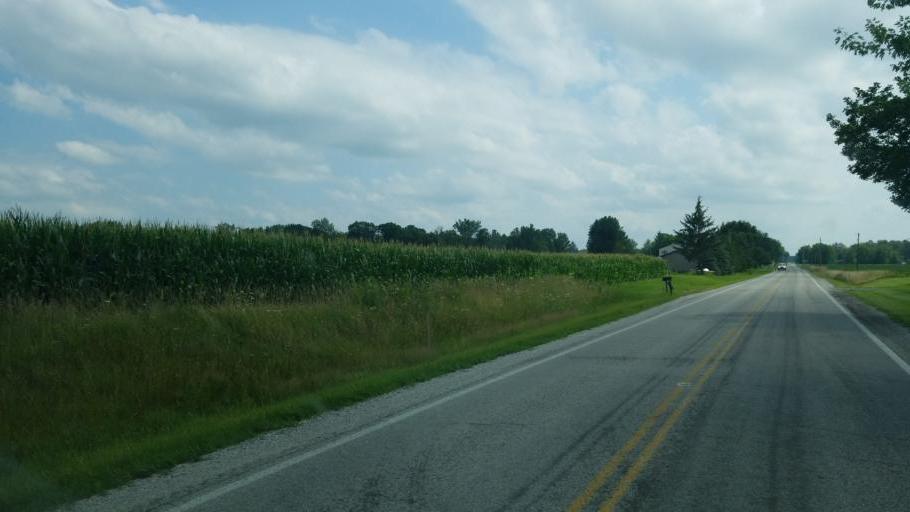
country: US
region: Ohio
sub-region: Crawford County
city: Crestline
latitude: 40.8341
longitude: -82.7873
